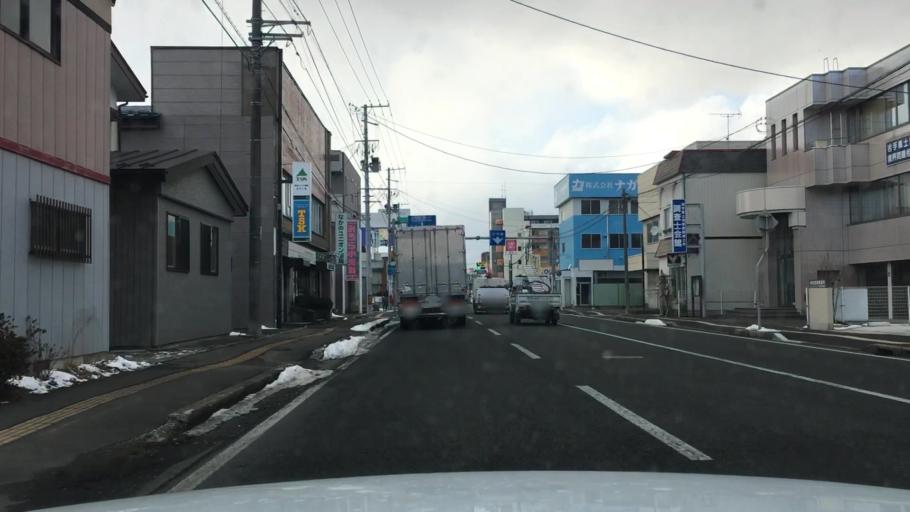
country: JP
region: Iwate
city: Morioka-shi
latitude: 39.6930
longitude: 141.1706
